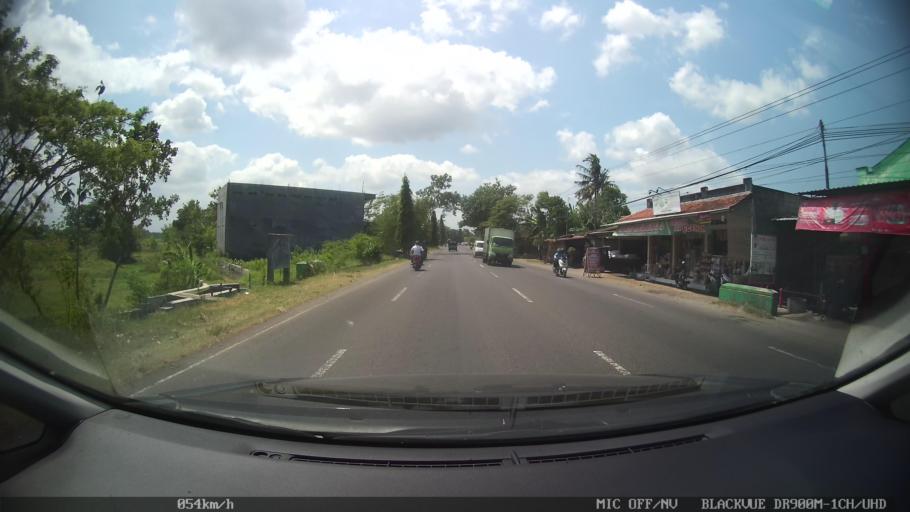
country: ID
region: Daerah Istimewa Yogyakarta
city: Pandak
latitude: -7.9087
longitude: 110.2999
